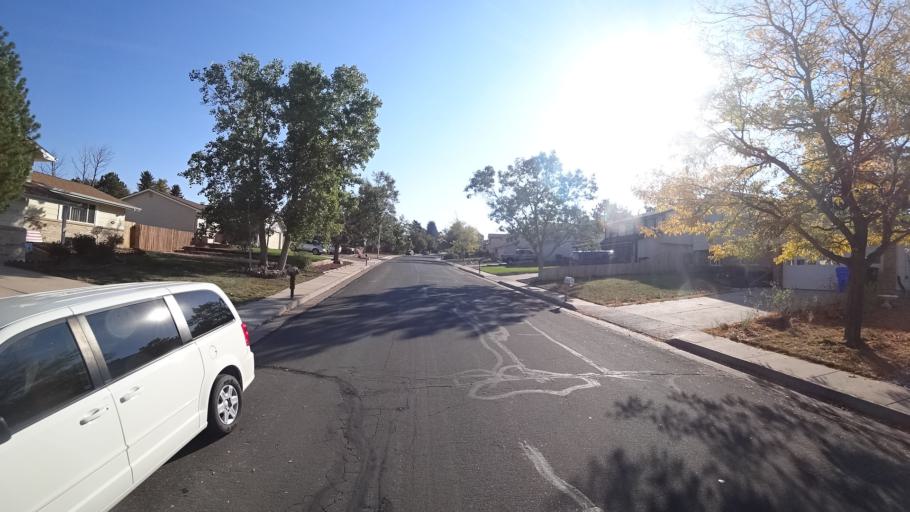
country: US
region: Colorado
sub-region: El Paso County
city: Cimarron Hills
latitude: 38.8883
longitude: -104.7307
